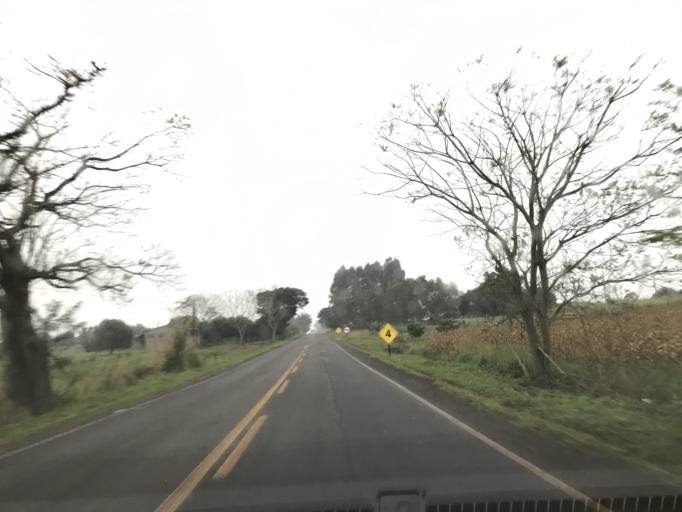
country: PY
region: Canindeyu
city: Salto del Guaira
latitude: -24.1266
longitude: -54.1160
